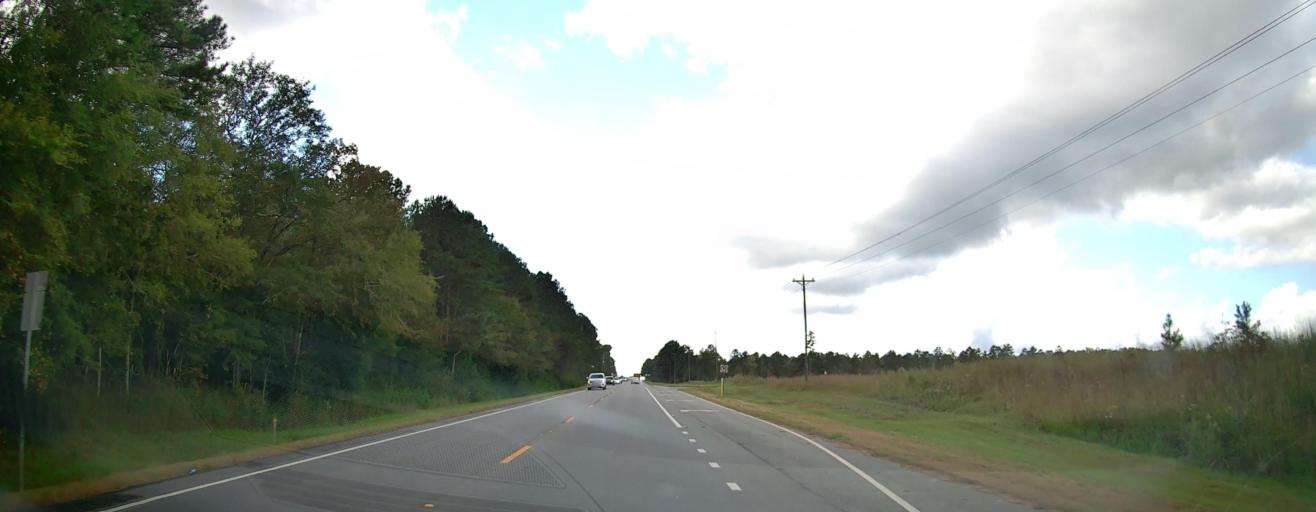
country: US
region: Georgia
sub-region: Baldwin County
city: Milledgeville
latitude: 33.0838
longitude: -83.2951
